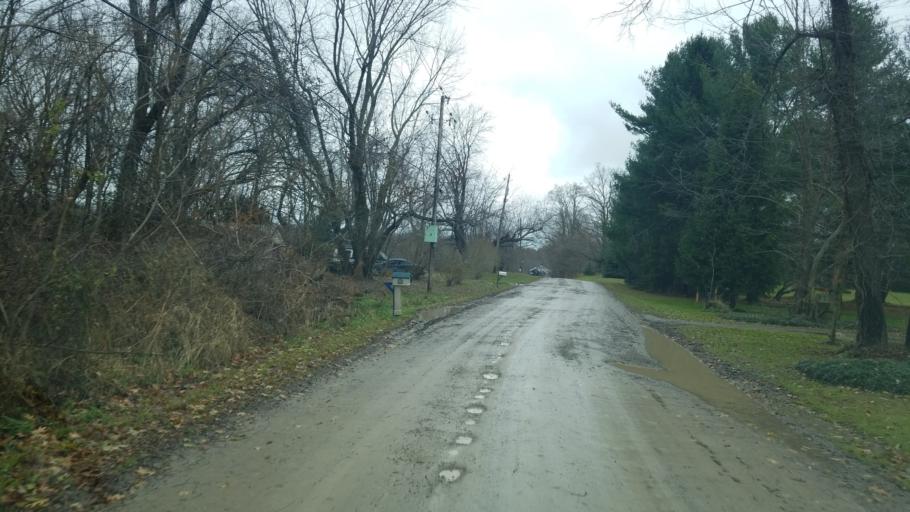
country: US
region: Ohio
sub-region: Ashtabula County
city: Conneaut
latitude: 41.9196
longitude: -80.6055
